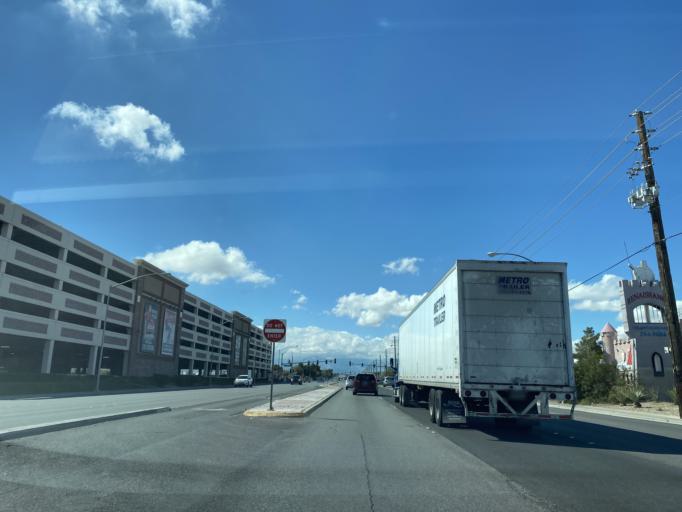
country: US
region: Nevada
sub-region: Clark County
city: North Las Vegas
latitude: 36.2398
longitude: -115.1187
